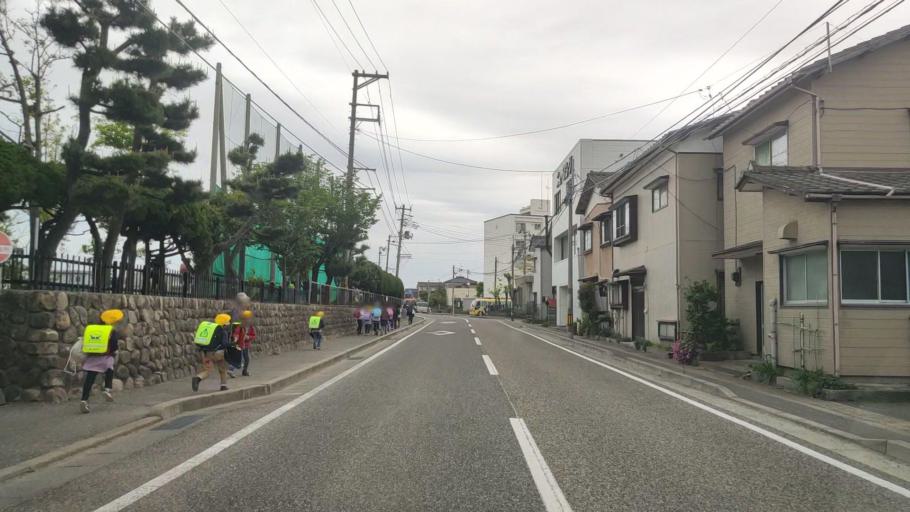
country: JP
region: Niigata
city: Niigata-shi
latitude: 37.9441
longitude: 139.0777
